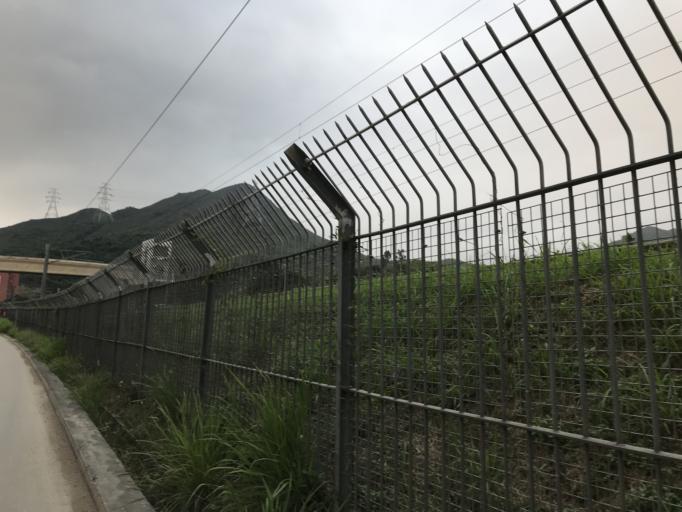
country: HK
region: Tai Po
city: Tai Po
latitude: 22.4796
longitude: 114.1550
